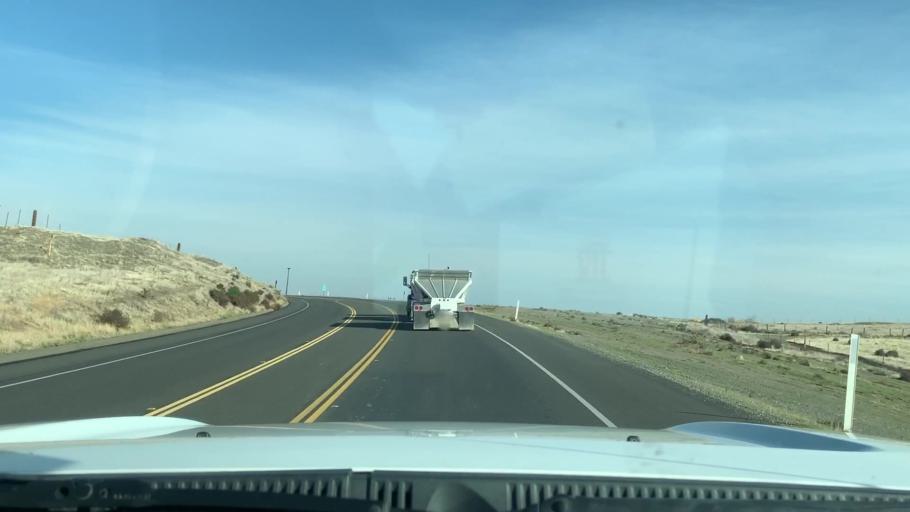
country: US
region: California
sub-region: Fresno County
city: Coalinga
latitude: 36.2094
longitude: -120.3121
